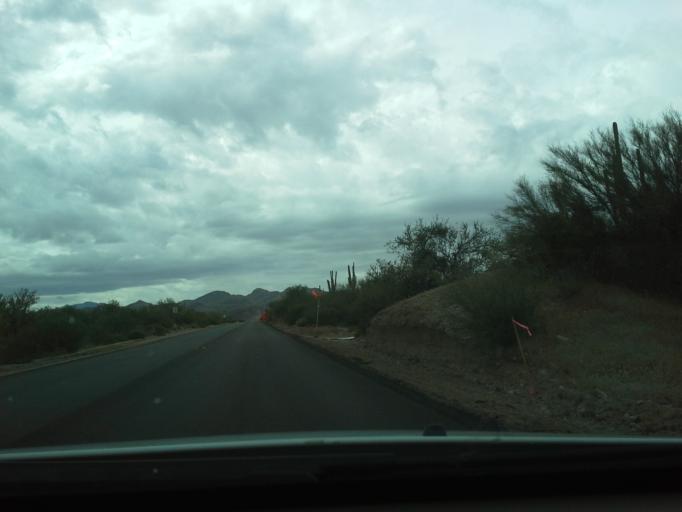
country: US
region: Arizona
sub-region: Maricopa County
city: Fountain Hills
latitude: 33.5912
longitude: -111.5432
